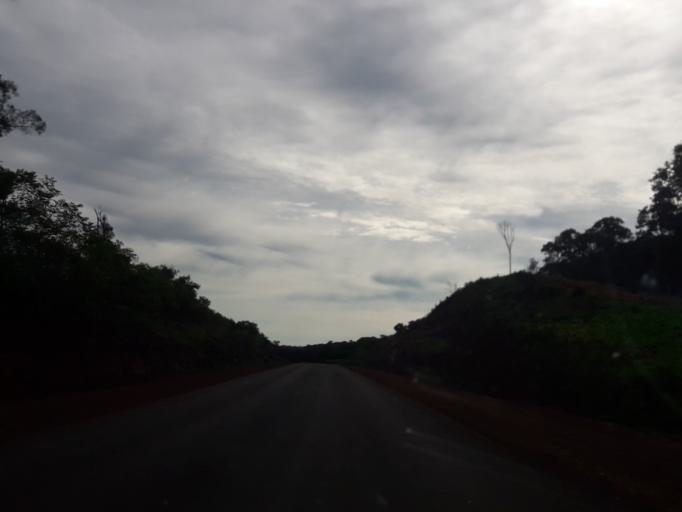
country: AR
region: Misiones
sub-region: Departamento de San Pedro
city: San Pedro
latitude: -26.5107
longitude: -53.9061
